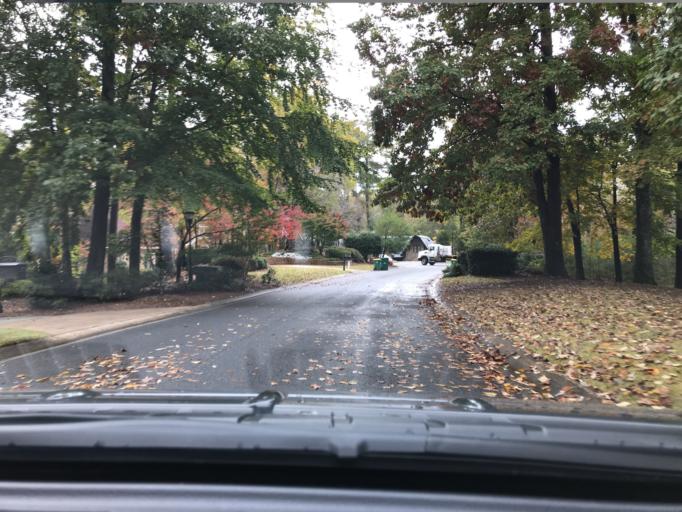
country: US
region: Georgia
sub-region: Fulton County
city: Johns Creek
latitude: 34.0045
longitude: -84.2409
